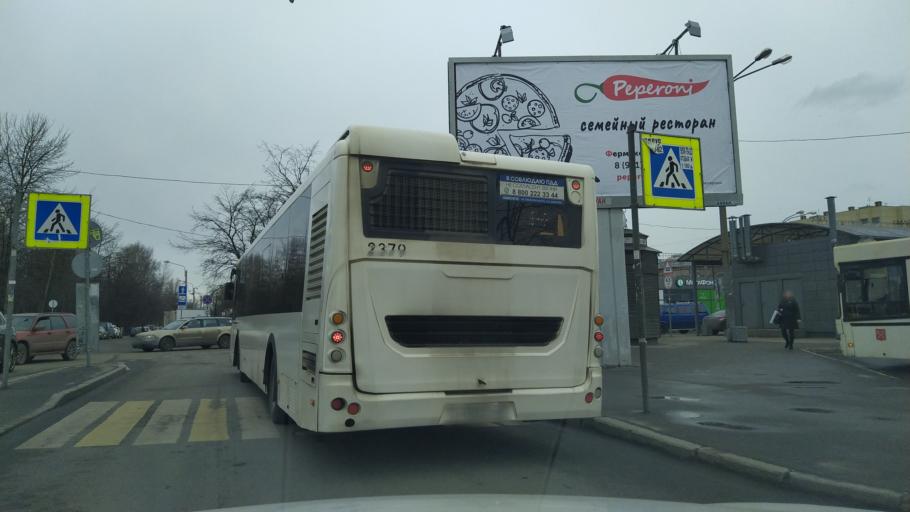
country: RU
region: Leningrad
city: Udel'naya
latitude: 60.0172
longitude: 30.3121
